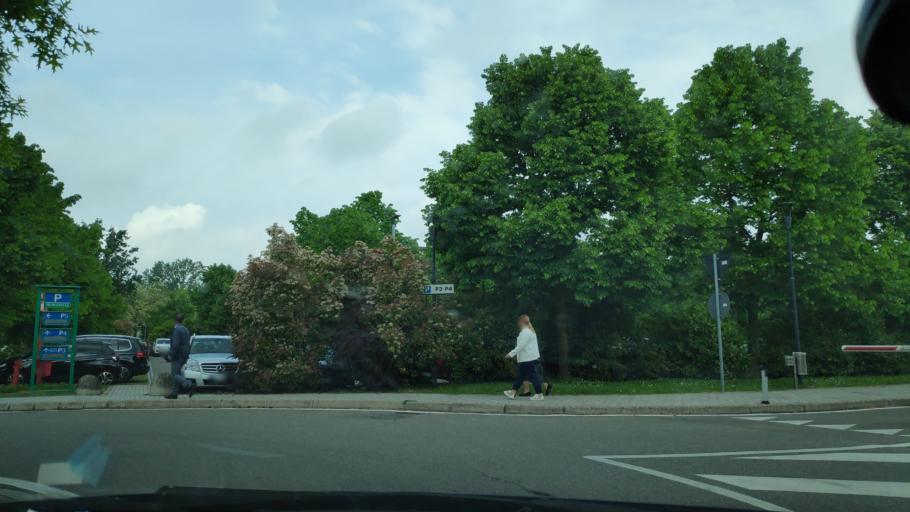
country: IT
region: Lombardy
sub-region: Citta metropolitana di Milano
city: Rozzano
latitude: 45.3725
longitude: 9.1668
